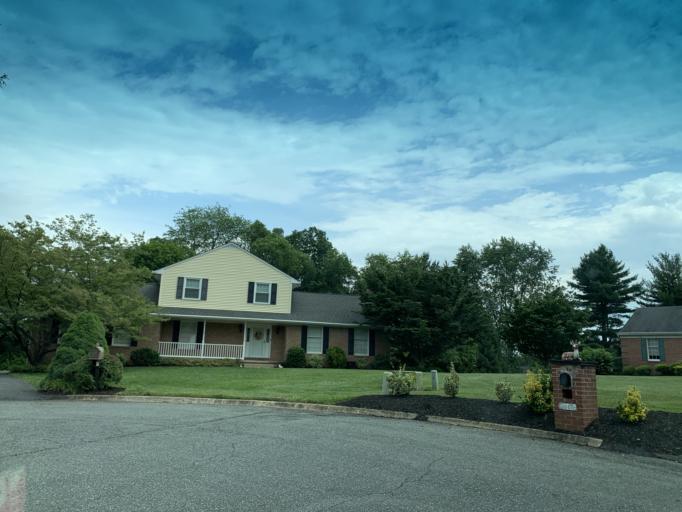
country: US
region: Maryland
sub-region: Harford County
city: Fallston
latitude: 39.5420
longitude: -76.4326
